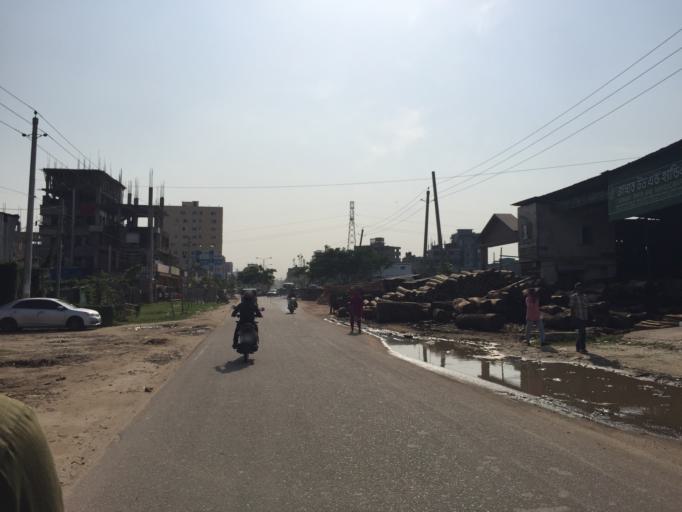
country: BD
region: Dhaka
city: Paltan
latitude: 23.7992
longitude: 90.4395
